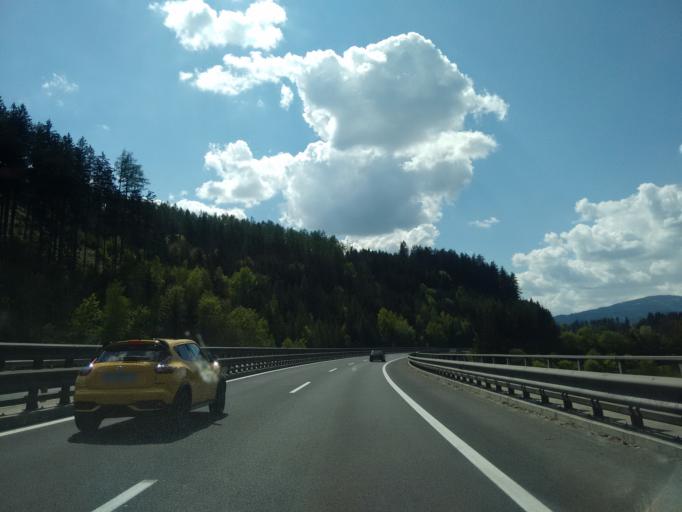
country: AT
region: Styria
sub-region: Politischer Bezirk Leoben
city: Sankt Michael in Obersteiermark
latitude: 47.3378
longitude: 15.0424
